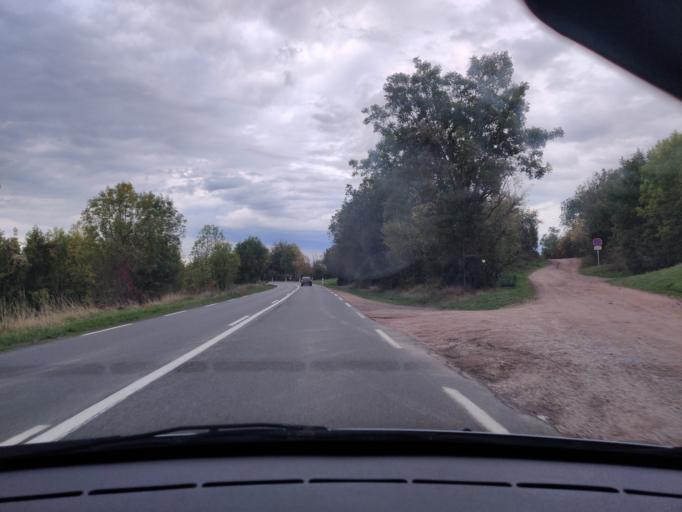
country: FR
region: Auvergne
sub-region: Departement du Puy-de-Dome
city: Saint-Bonnet-pres-Riom
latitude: 45.9204
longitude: 3.1219
